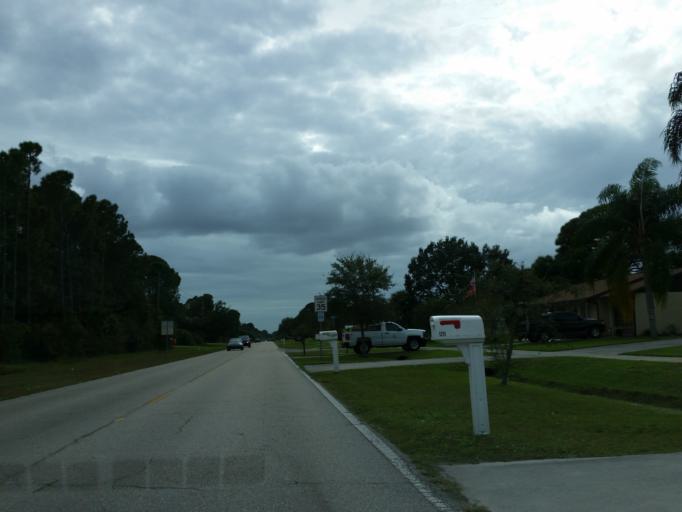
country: US
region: Florida
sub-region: Sarasota County
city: North Port
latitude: 27.0672
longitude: -82.1977
